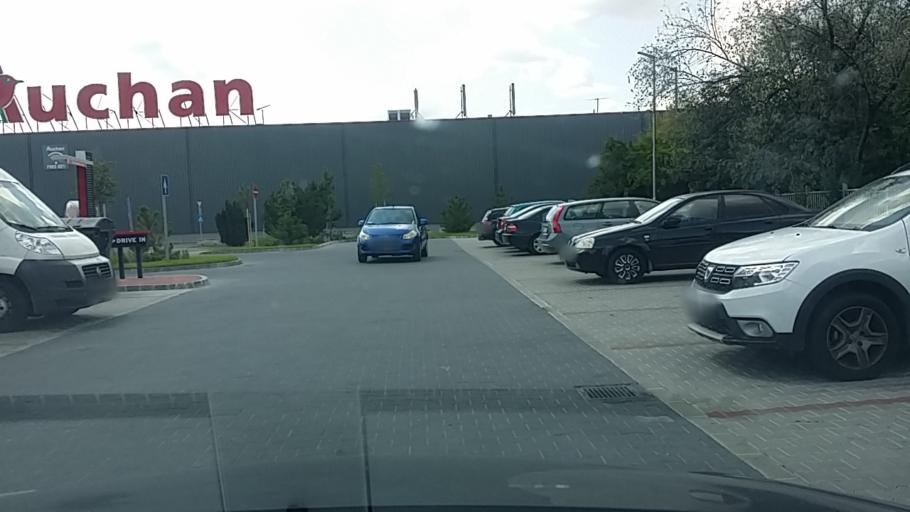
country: HU
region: Pest
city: Budaors
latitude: 47.4556
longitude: 18.9464
